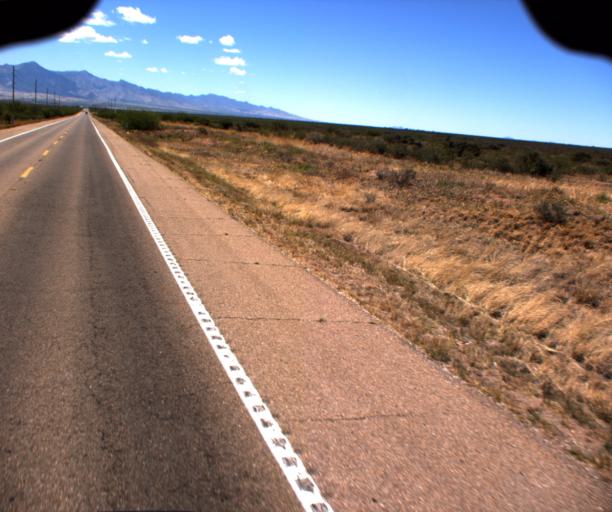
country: US
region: Arizona
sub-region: Cochise County
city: Naco
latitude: 31.3744
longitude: -109.9958
